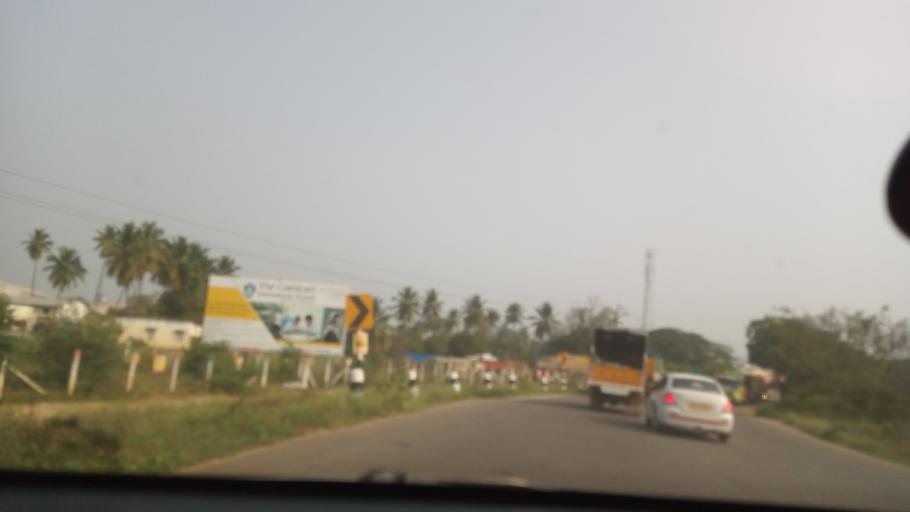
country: IN
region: Tamil Nadu
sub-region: Coimbatore
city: Annur
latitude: 11.1892
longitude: 77.0637
